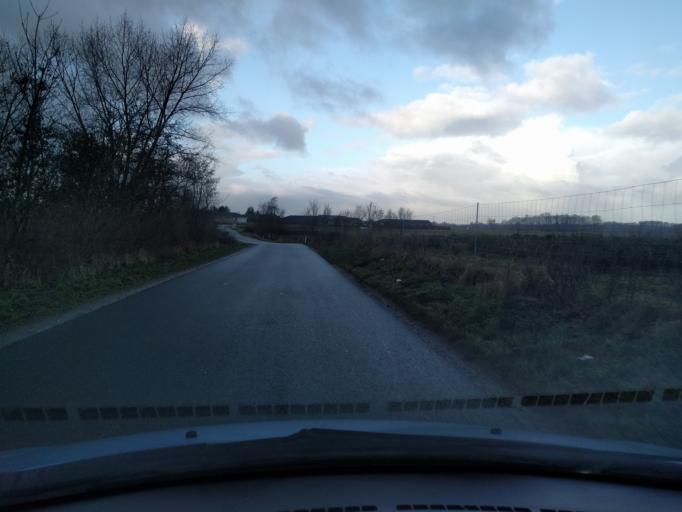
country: DK
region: South Denmark
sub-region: Kerteminde Kommune
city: Langeskov
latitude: 55.3791
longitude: 10.5780
